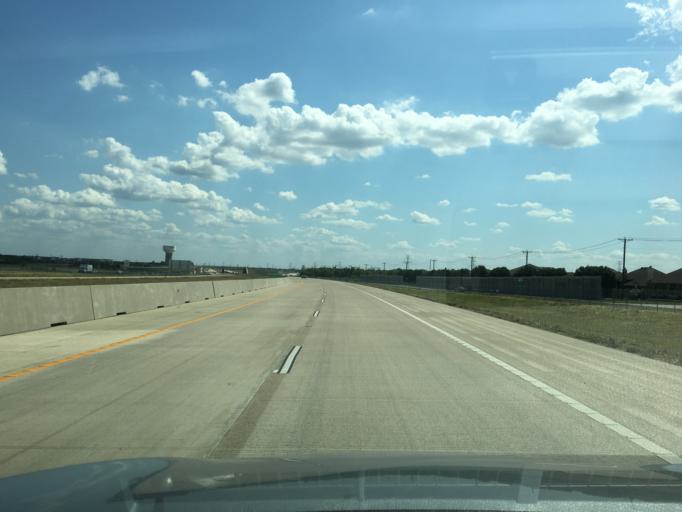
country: US
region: Texas
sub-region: Tarrant County
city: Mansfield
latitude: 32.6178
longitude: -97.0760
